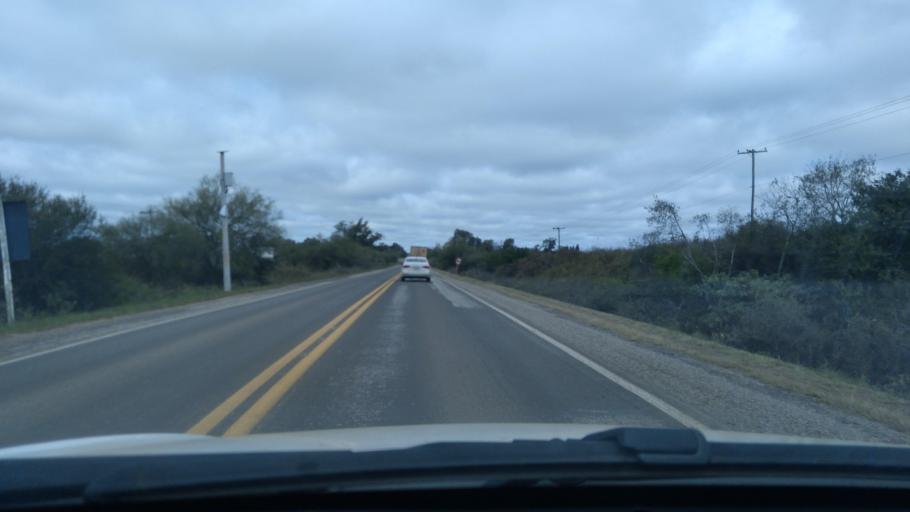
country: BR
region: Rio Grande do Sul
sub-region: Dom Pedrito
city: Dom Pedrito
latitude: -30.9801
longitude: -54.6428
